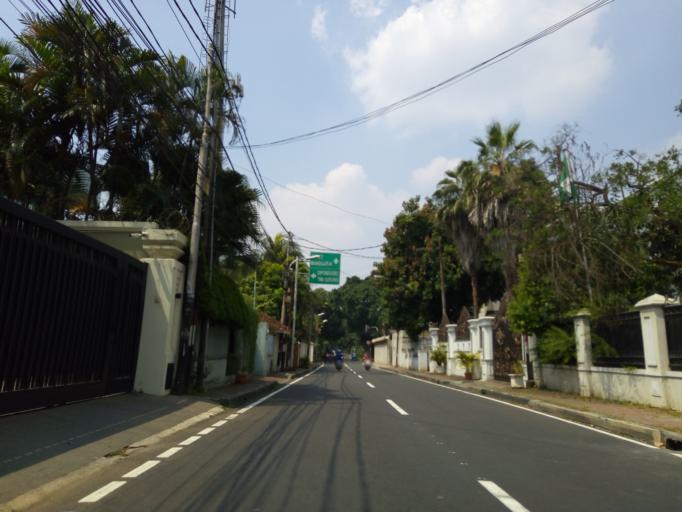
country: ID
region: Jakarta Raya
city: Jakarta
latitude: -6.2020
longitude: 106.8370
